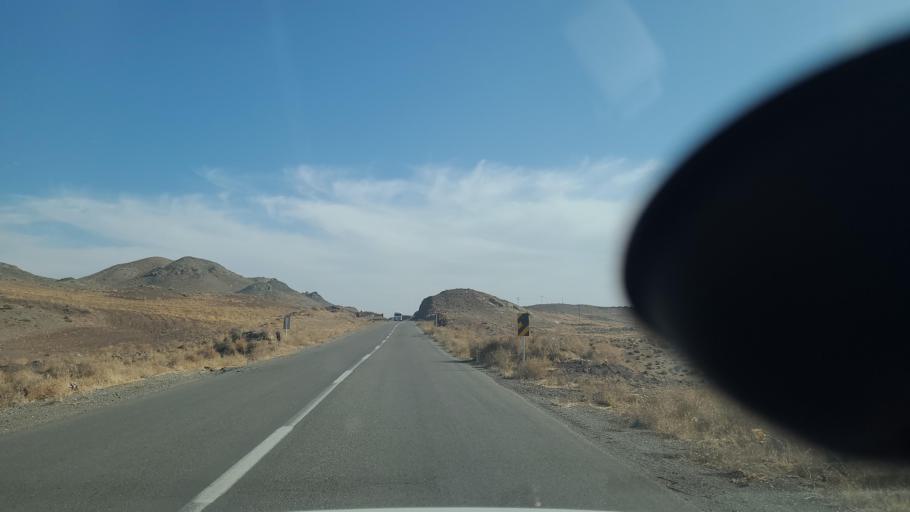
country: IR
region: Razavi Khorasan
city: Fariman
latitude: 35.5946
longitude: 59.7123
